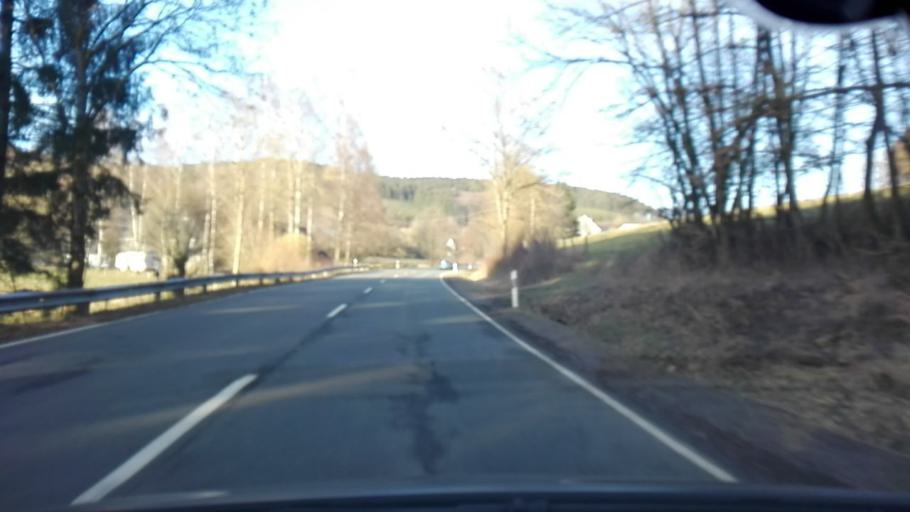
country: DE
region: North Rhine-Westphalia
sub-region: Regierungsbezirk Arnsberg
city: Lennestadt
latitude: 51.1852
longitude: 8.1078
